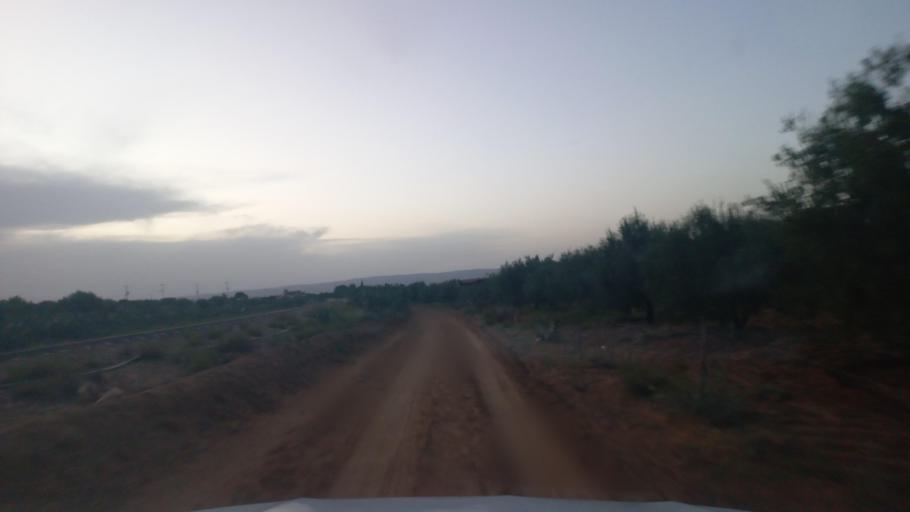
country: TN
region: Al Qasrayn
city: Kasserine
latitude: 35.2304
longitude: 9.0355
